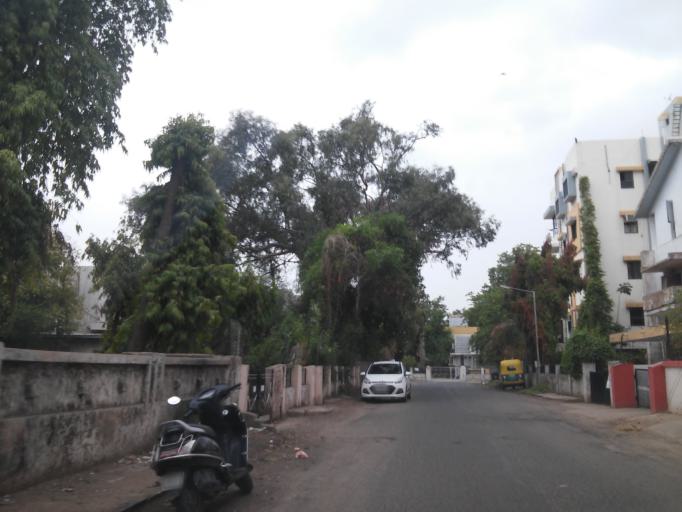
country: IN
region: Gujarat
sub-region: Ahmadabad
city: Ahmedabad
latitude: 23.0120
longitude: 72.5607
